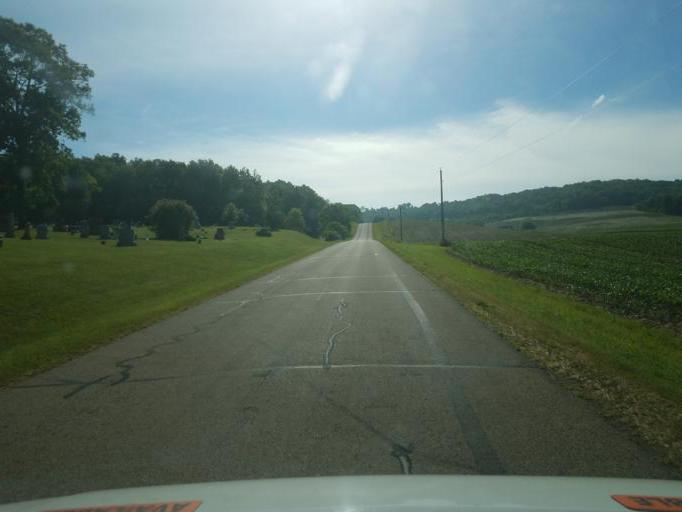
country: US
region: Wisconsin
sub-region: Sauk County
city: Reedsburg
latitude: 43.5479
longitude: -90.1211
